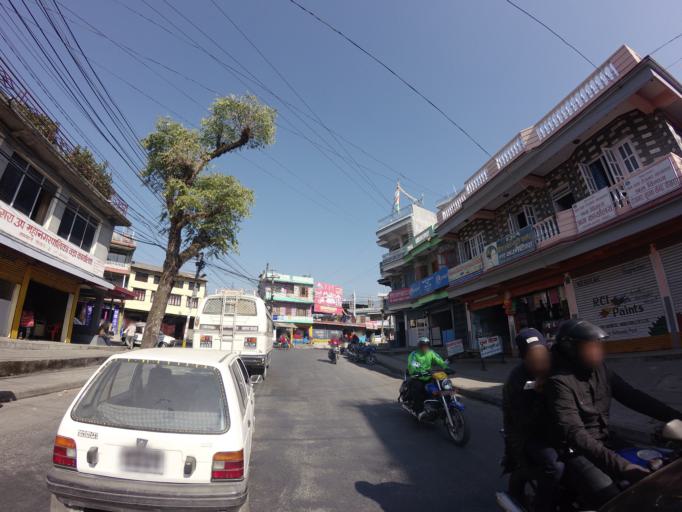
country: NP
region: Western Region
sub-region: Gandaki Zone
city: Pokhara
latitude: 28.2293
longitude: 83.9909
